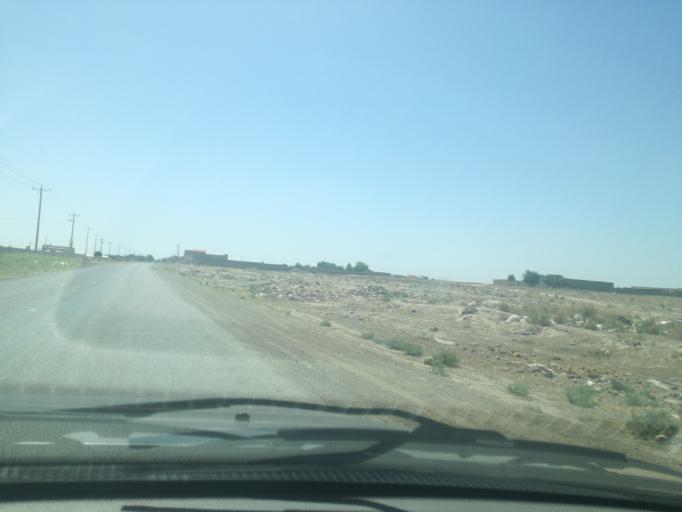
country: IR
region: Razavi Khorasan
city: Sarakhs
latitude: 36.5681
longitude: 61.1392
